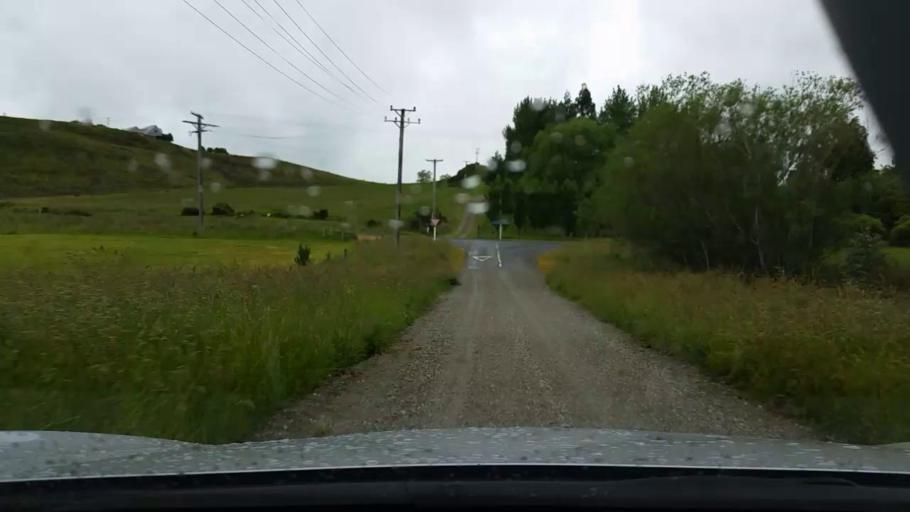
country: NZ
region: Southland
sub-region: Gore District
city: Gore
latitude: -46.0808
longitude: 168.9556
